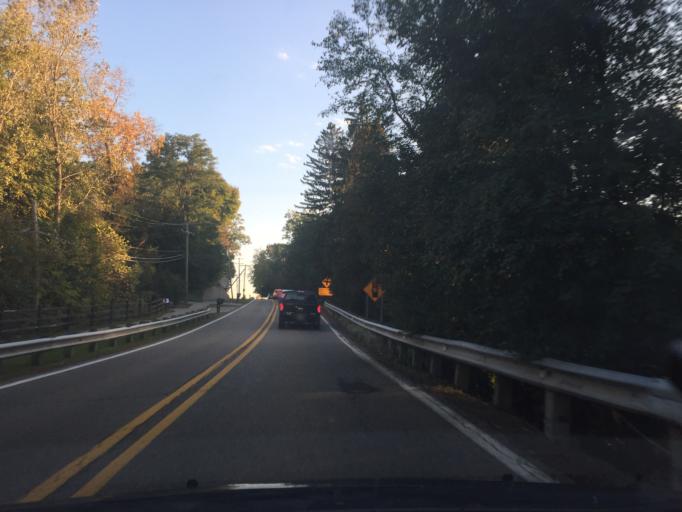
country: US
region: Michigan
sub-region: Oakland County
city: Bloomfield Hills
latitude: 42.5836
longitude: -83.2867
